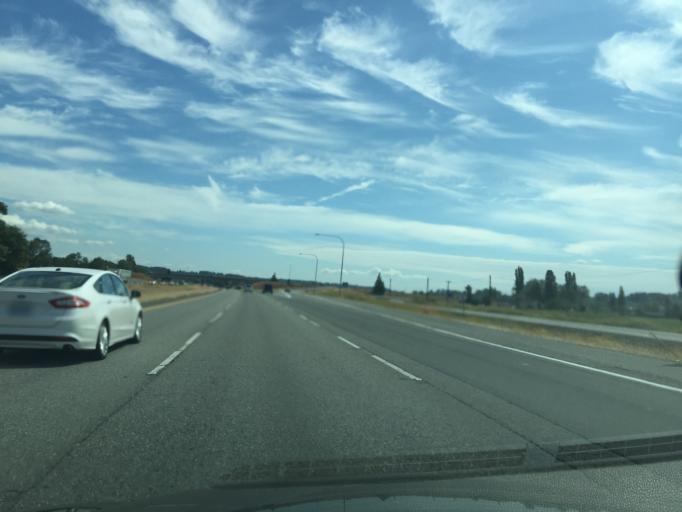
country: US
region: Washington
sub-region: Skagit County
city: Mount Vernon
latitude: 48.3454
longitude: -122.3363
